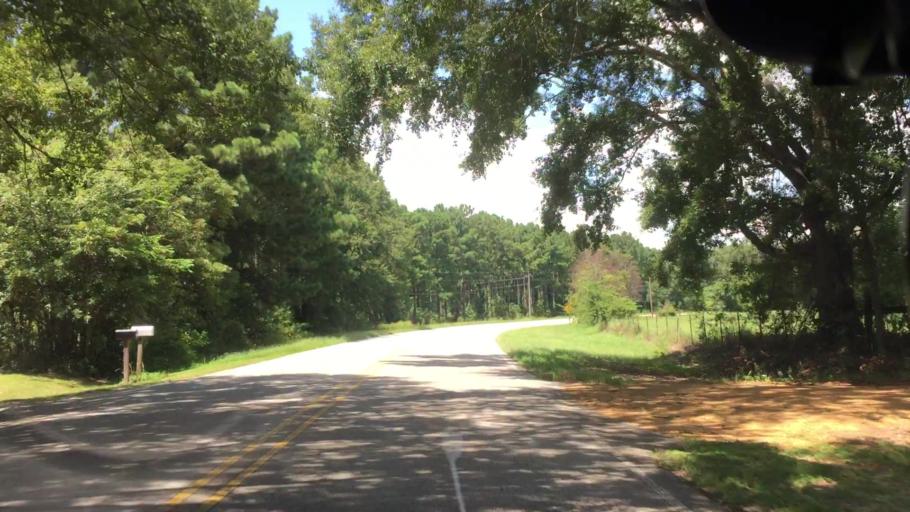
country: US
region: Alabama
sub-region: Pike County
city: Troy
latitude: 31.7534
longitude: -85.9849
